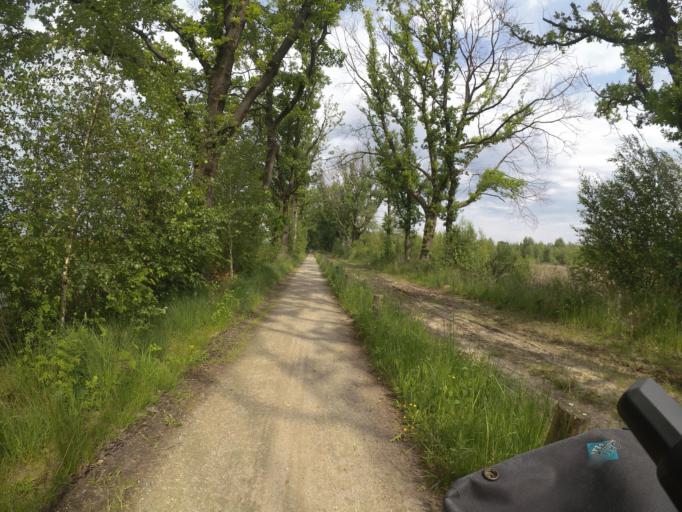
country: NL
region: Drenthe
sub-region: Gemeente Assen
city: Assen
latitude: 53.0034
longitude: 6.4457
